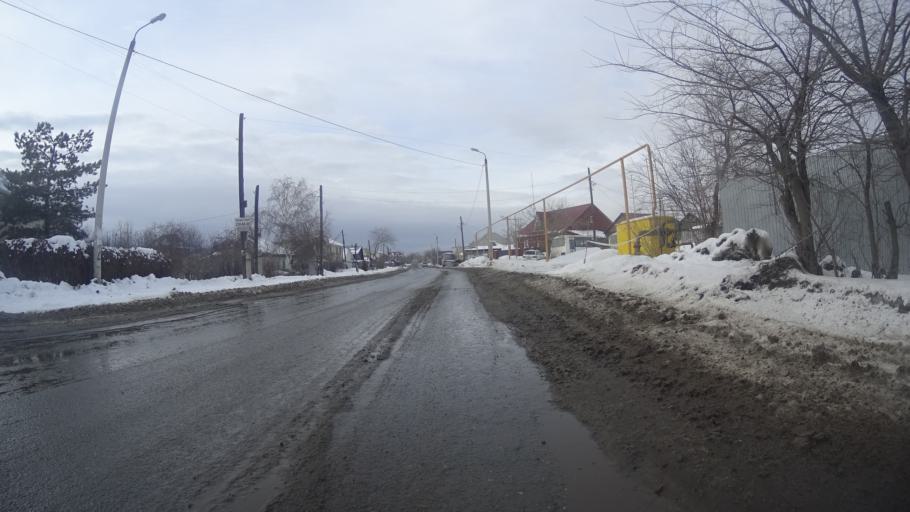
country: RU
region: Chelyabinsk
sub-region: Gorod Chelyabinsk
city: Chelyabinsk
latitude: 55.1287
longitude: 61.3924
